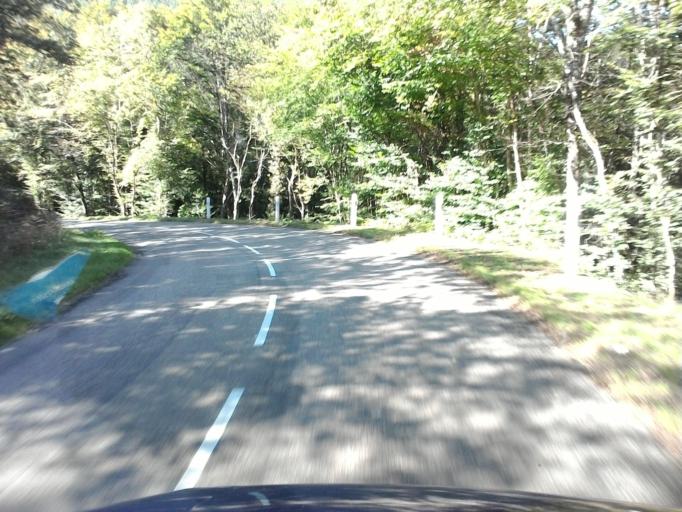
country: FR
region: Bourgogne
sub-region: Departement de la Nievre
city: Lormes
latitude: 47.2162
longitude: 3.9347
